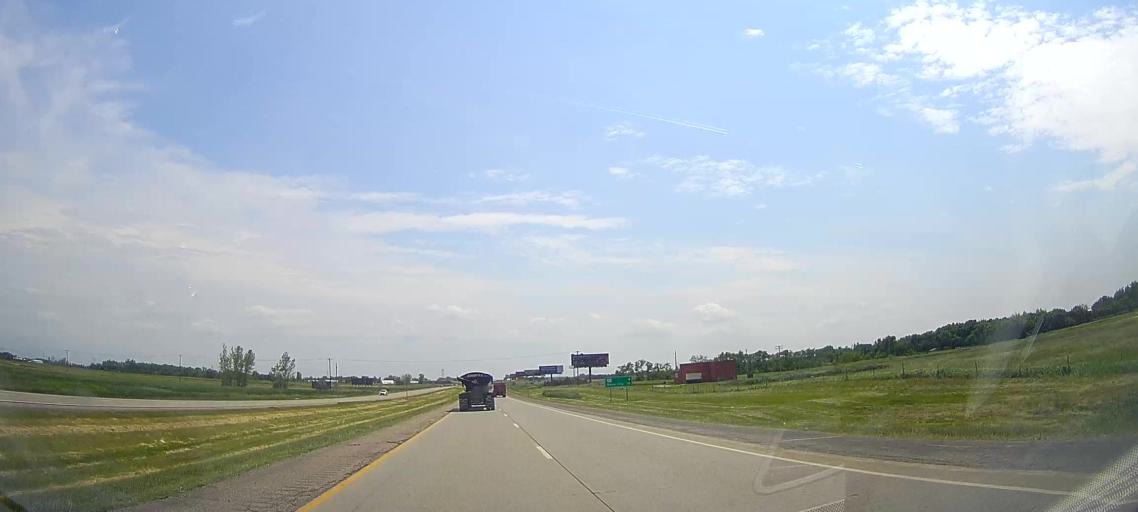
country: US
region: South Dakota
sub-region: Lincoln County
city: Tea
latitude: 43.4482
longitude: -96.7979
